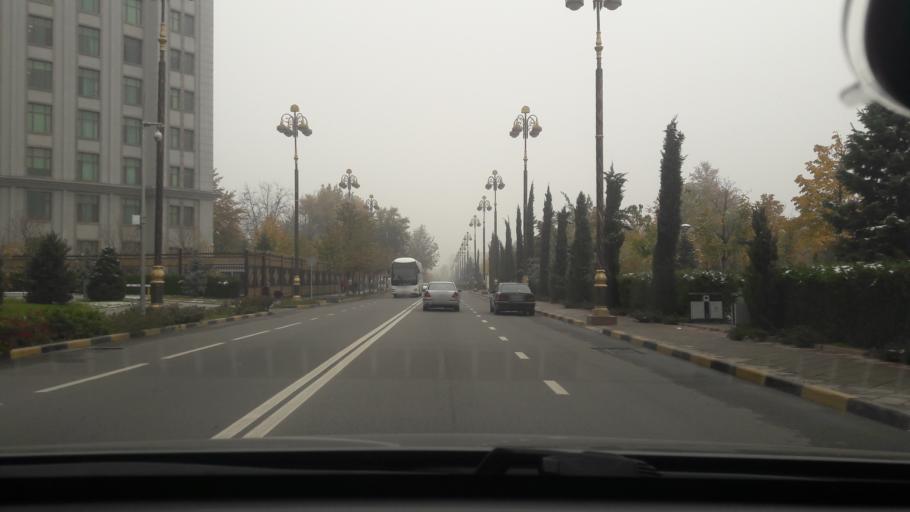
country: TJ
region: Dushanbe
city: Dushanbe
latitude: 38.5794
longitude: 68.7822
